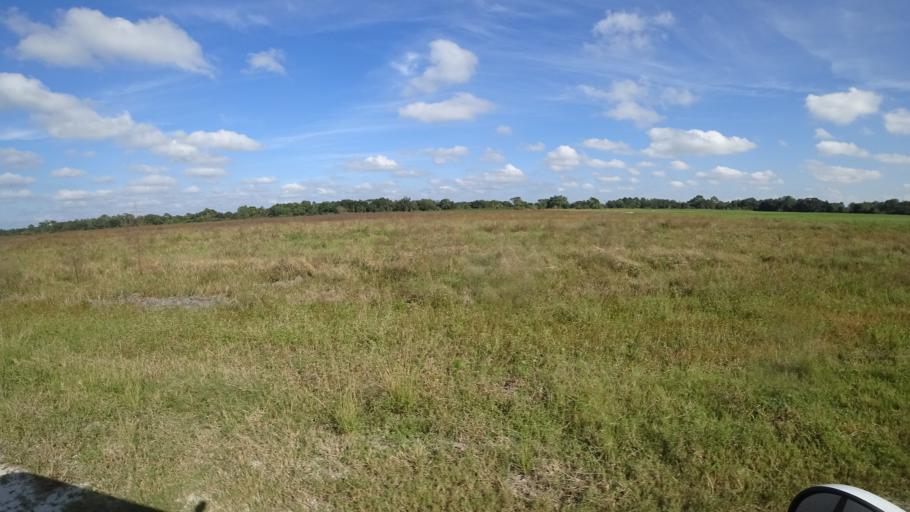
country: US
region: Florida
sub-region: Sarasota County
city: Lake Sarasota
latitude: 27.3637
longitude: -82.1574
